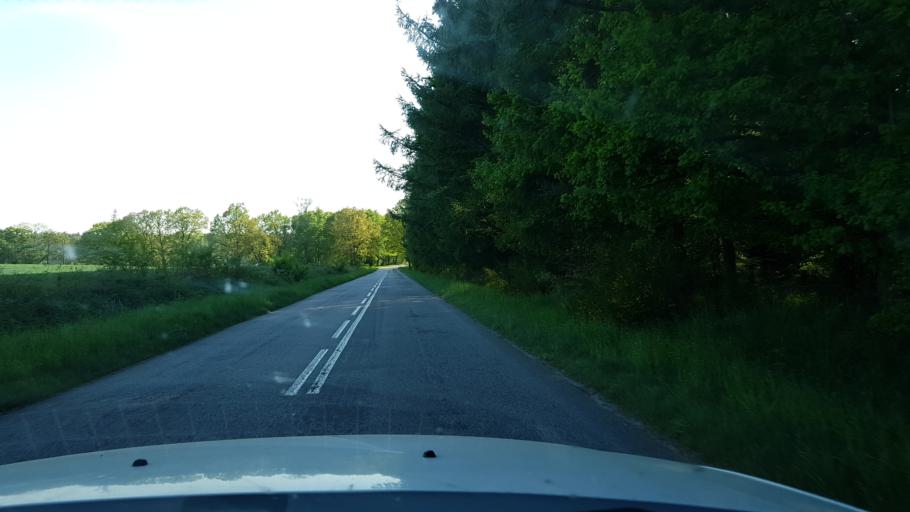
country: PL
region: West Pomeranian Voivodeship
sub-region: Powiat lobeski
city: Resko
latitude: 53.7362
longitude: 15.3572
